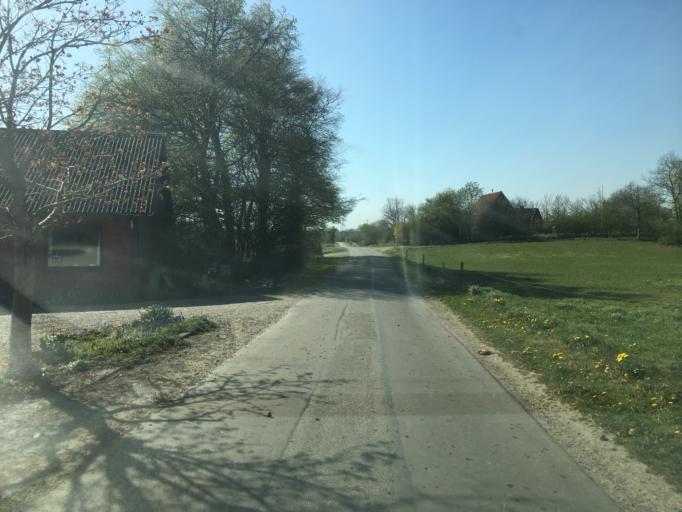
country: DK
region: South Denmark
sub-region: Aabenraa Kommune
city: Rodekro
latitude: 55.0964
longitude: 9.2471
